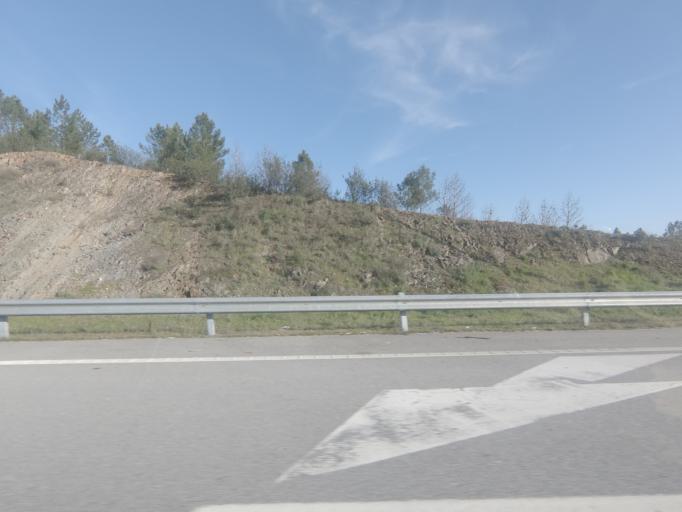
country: PT
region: Portalegre
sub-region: Nisa
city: Nisa
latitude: 39.5614
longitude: -7.7987
